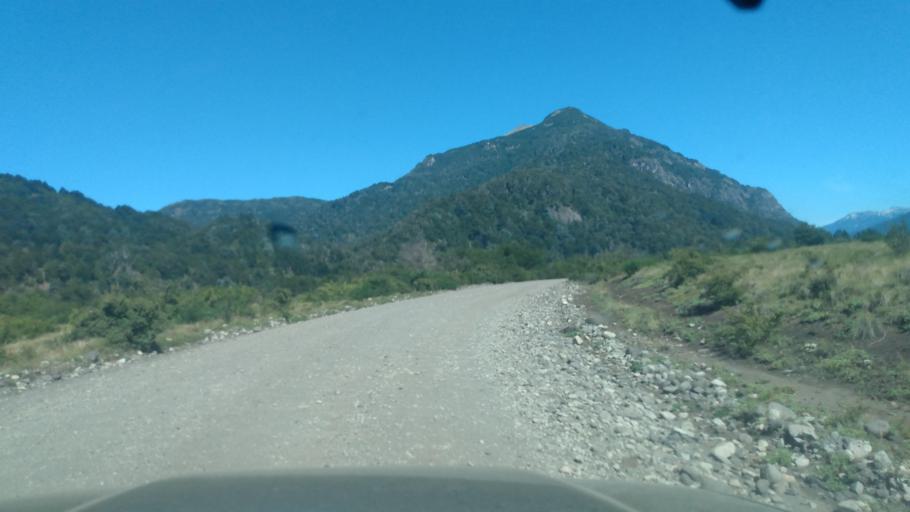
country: AR
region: Neuquen
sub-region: Departamento de Lacar
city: San Martin de los Andes
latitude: -39.7460
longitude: -71.5195
